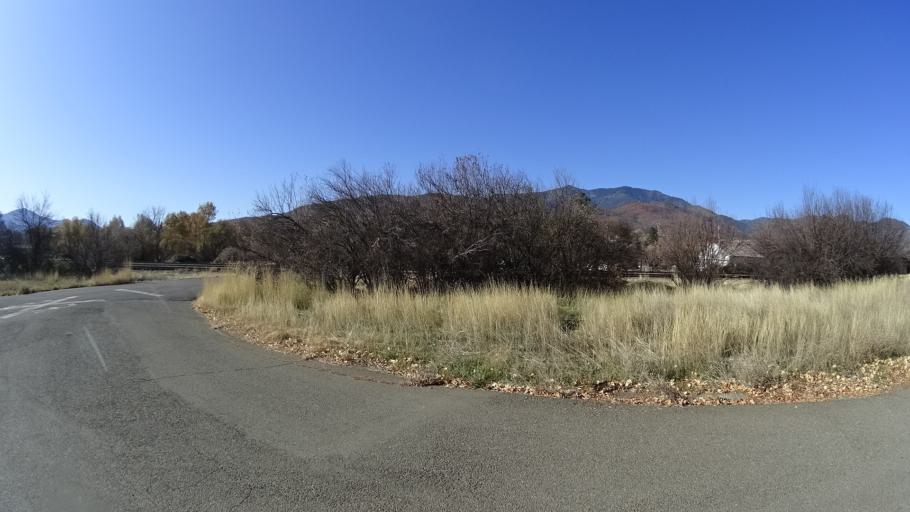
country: US
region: California
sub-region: Siskiyou County
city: Montague
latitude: 41.9121
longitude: -122.5565
